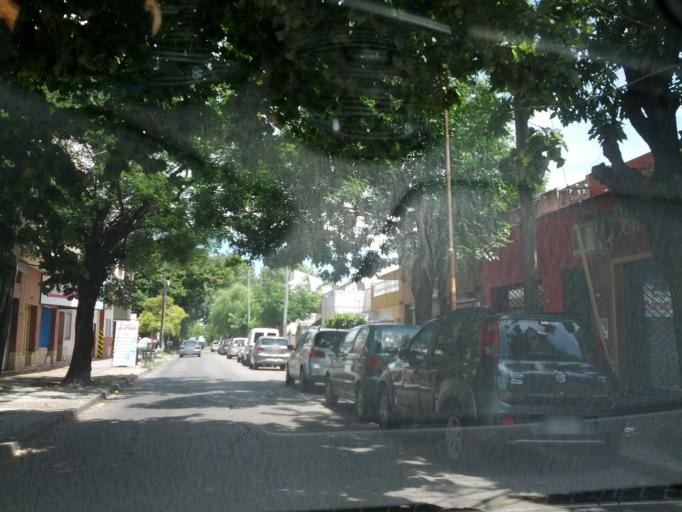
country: AR
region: Buenos Aires
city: San Justo
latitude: -34.6485
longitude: -58.5672
